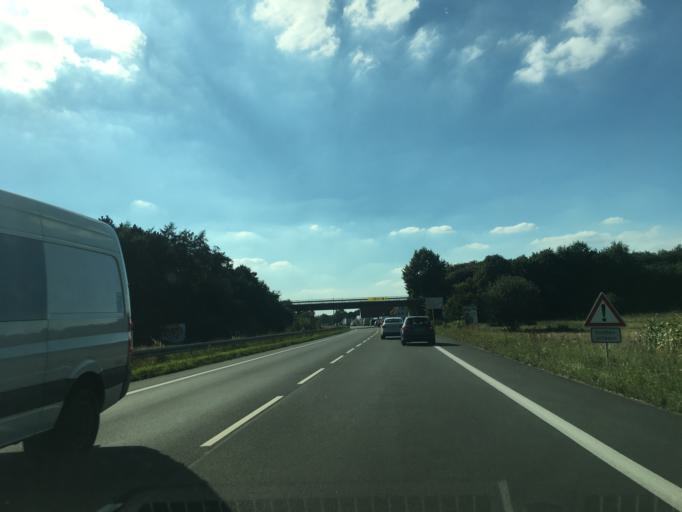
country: DE
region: North Rhine-Westphalia
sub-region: Regierungsbezirk Munster
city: Warendorf
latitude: 51.9489
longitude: 8.0187
